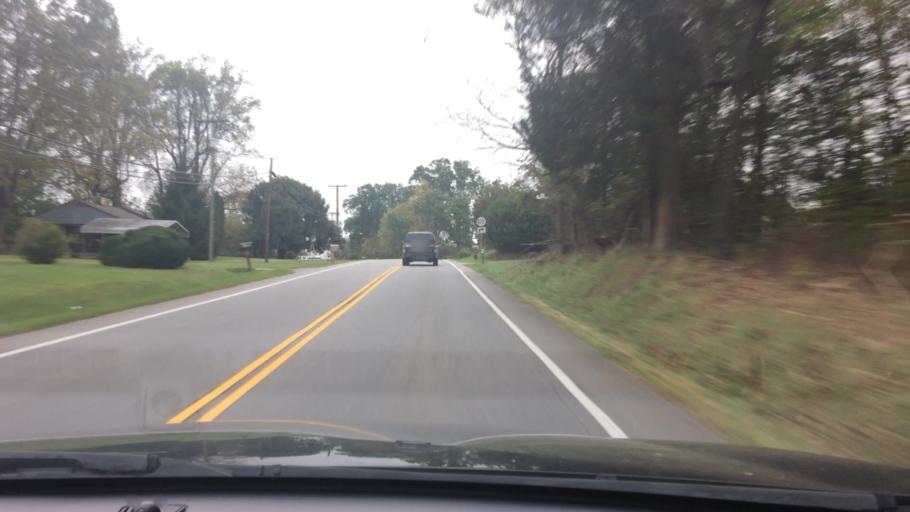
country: US
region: Virginia
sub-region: Franklin County
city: Henry Fork
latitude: 37.0162
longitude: -79.8299
